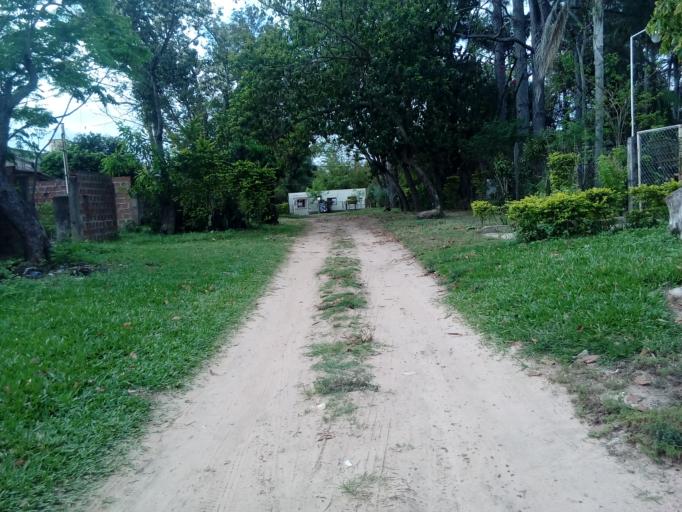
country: AR
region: Corrientes
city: San Luis del Palmar
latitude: -27.4587
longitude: -58.6554
